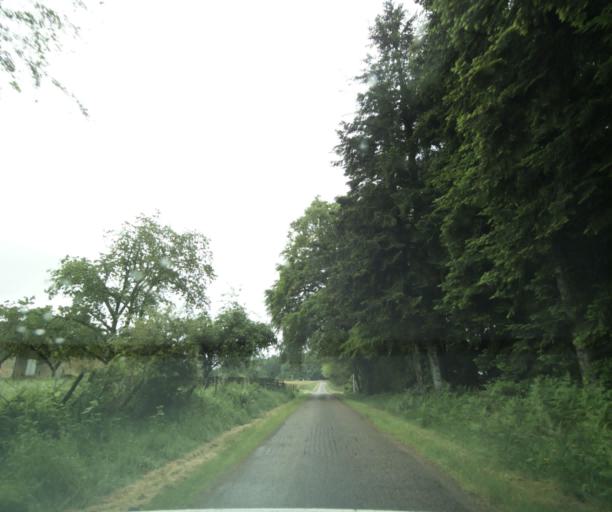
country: FR
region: Bourgogne
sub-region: Departement de Saone-et-Loire
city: Charolles
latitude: 46.4787
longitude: 4.4142
